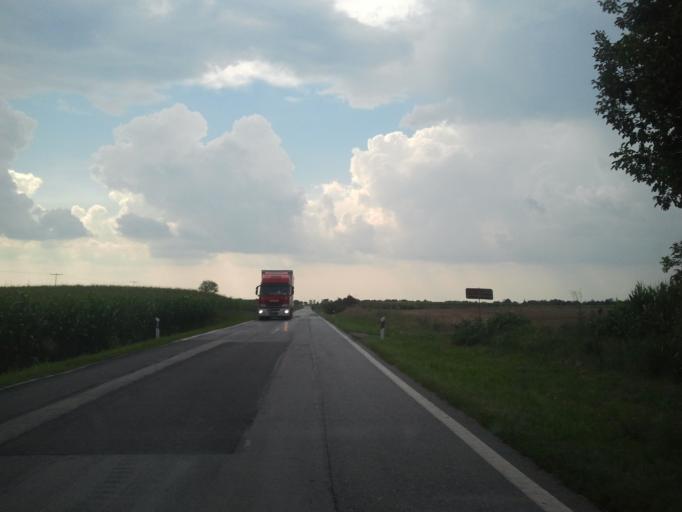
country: HR
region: Vukovarsko-Srijemska
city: Lovas
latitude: 45.2509
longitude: 19.2074
